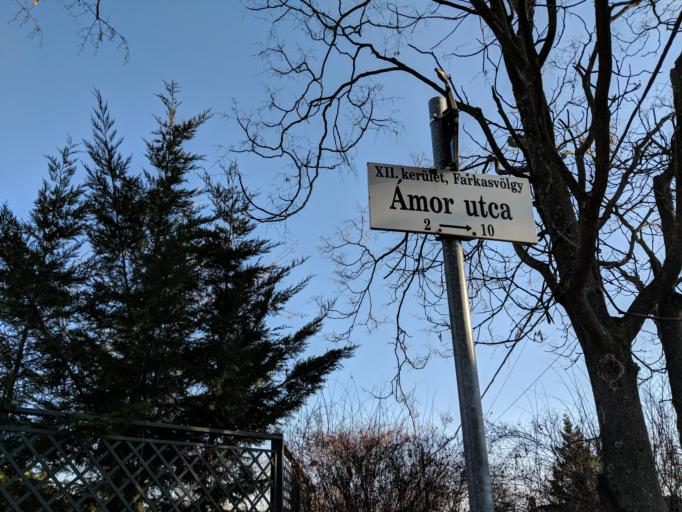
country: HU
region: Budapest
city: Budapest XII. keruelet
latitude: 47.4850
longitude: 18.9891
